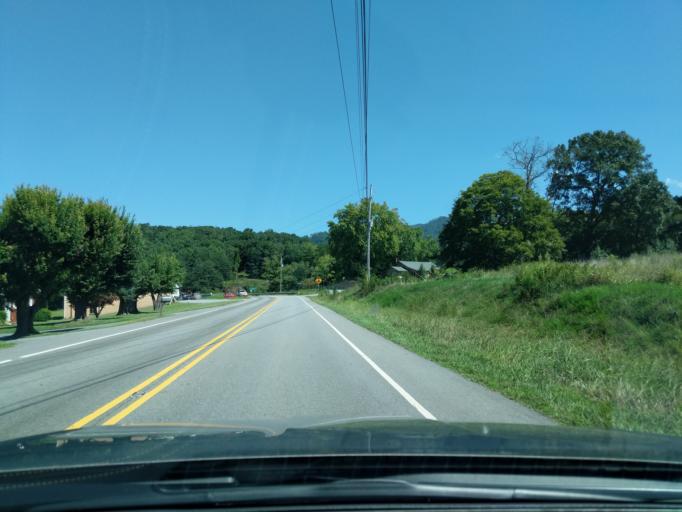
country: US
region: Georgia
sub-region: Towns County
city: Hiawassee
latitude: 35.0220
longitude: -83.7315
